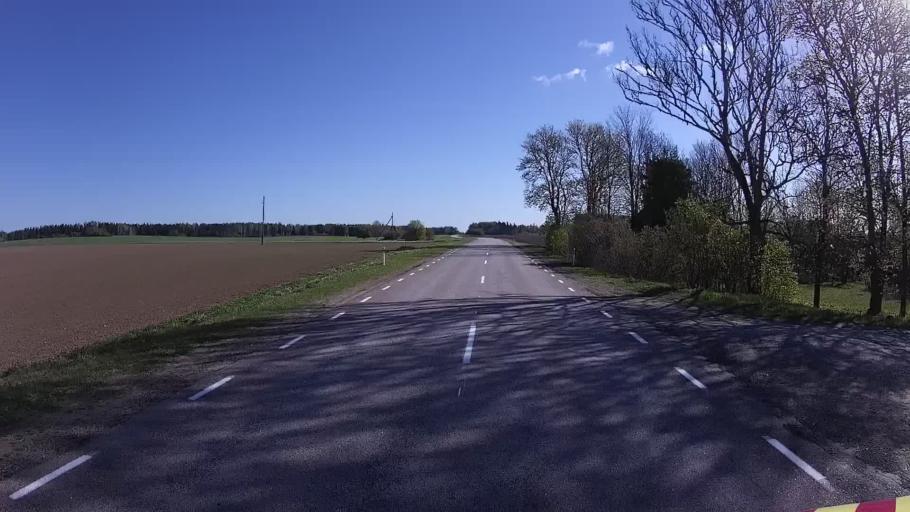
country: EE
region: Jaervamaa
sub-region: Jaerva-Jaani vald
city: Jarva-Jaani
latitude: 58.9248
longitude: 25.8986
